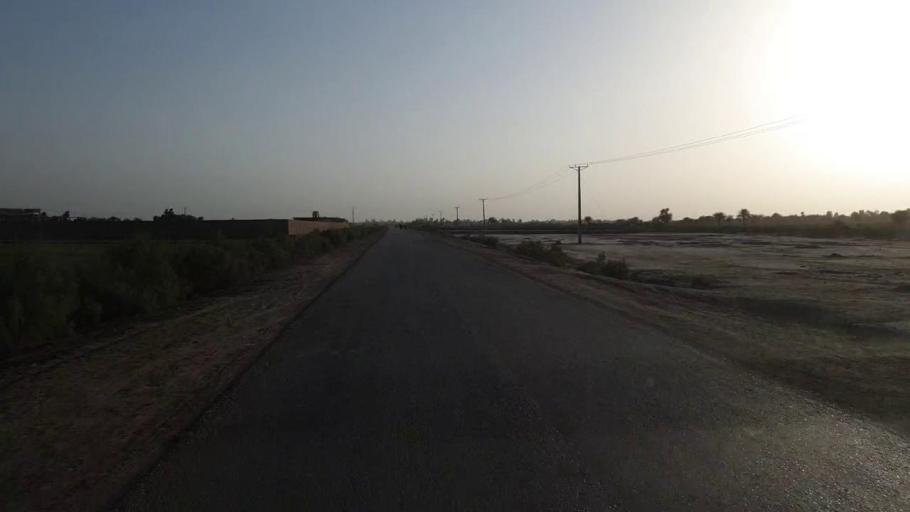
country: PK
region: Sindh
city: Jam Sahib
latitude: 26.2818
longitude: 68.5806
